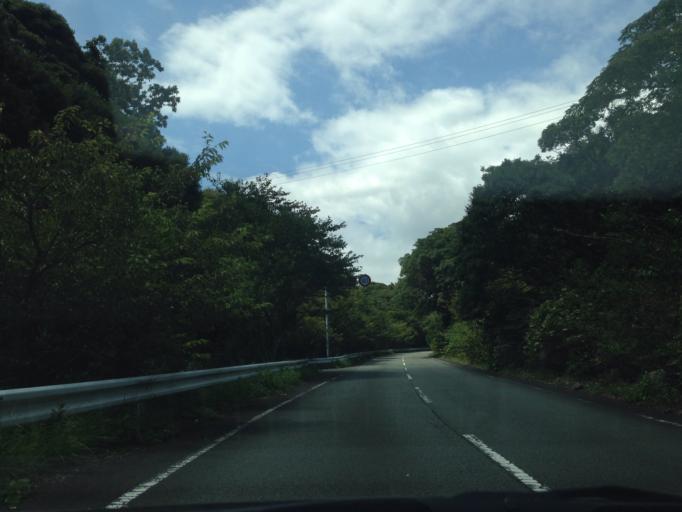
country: JP
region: Shizuoka
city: Shimoda
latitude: 34.6296
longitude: 138.8223
